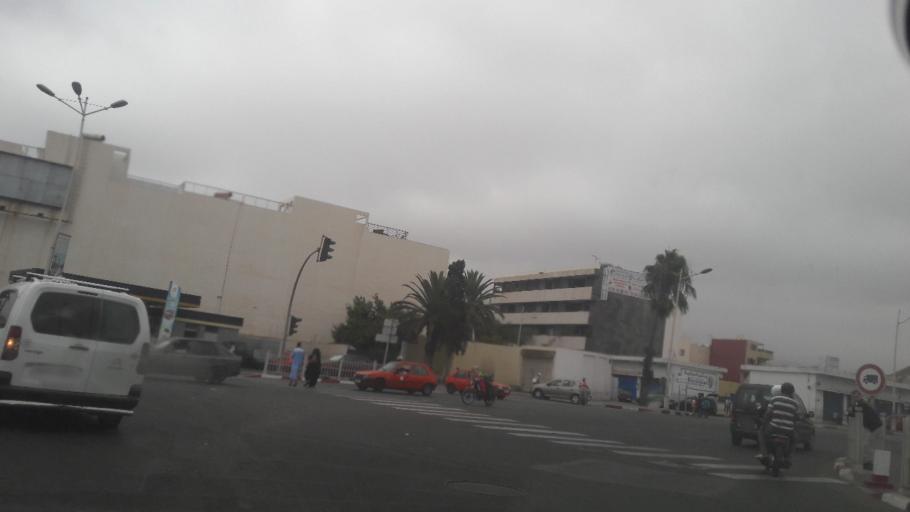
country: MA
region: Souss-Massa-Draa
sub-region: Agadir-Ida-ou-Tnan
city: Agadir
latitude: 30.4117
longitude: -9.5909
